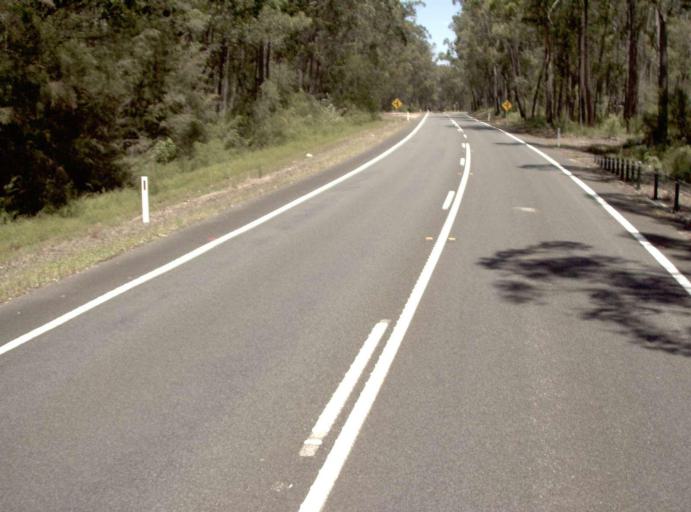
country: AU
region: Victoria
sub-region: East Gippsland
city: Lakes Entrance
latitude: -37.7509
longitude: 148.0685
